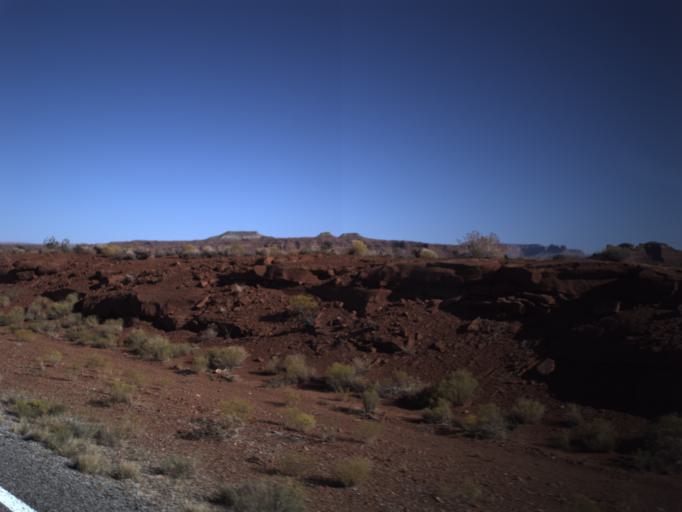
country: US
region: Utah
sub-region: San Juan County
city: Blanding
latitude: 37.8004
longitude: -110.3069
